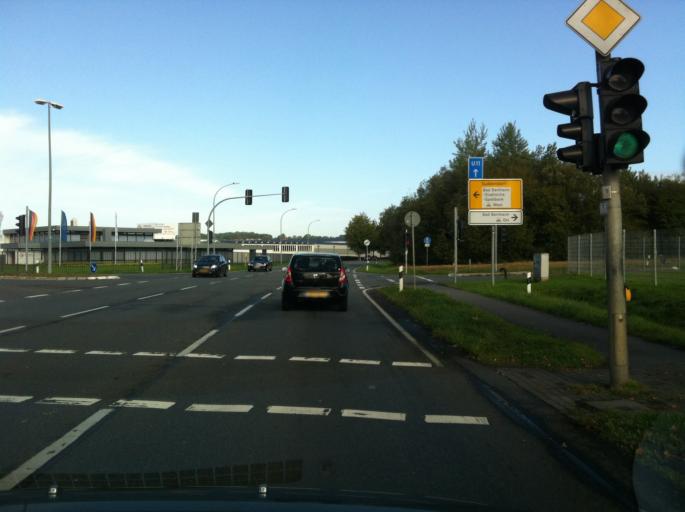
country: DE
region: Lower Saxony
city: Bad Bentheim
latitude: 52.2882
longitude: 7.1793
